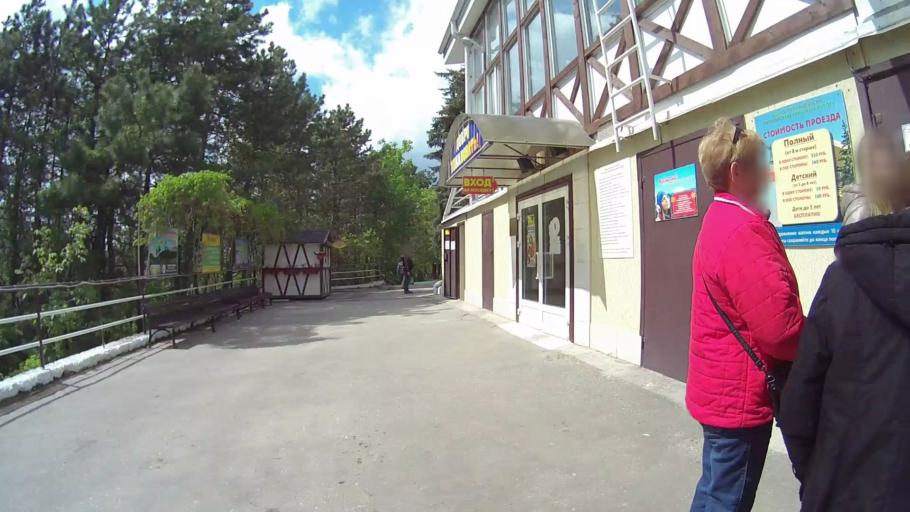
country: RU
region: Stavropol'skiy
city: Pyatigorsk
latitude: 44.0436
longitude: 43.0813
